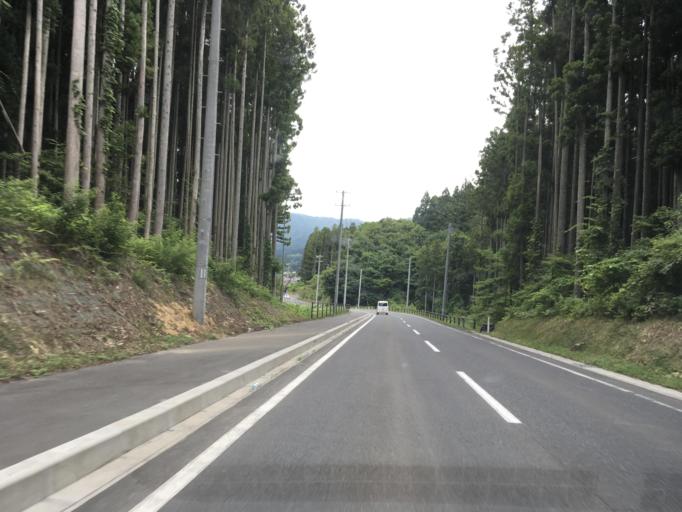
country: JP
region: Iwate
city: Ichinoseki
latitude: 38.9322
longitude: 141.4390
